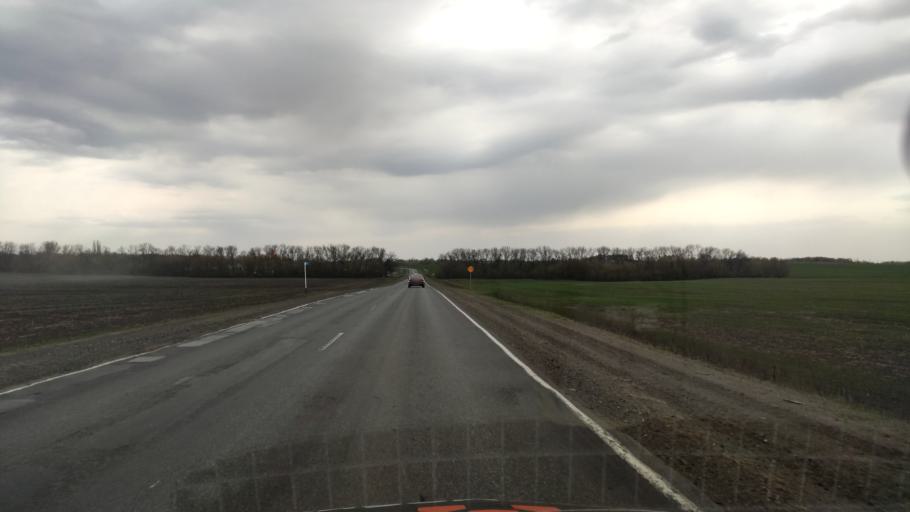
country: RU
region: Kursk
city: Gorshechnoye
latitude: 51.5431
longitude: 38.0257
